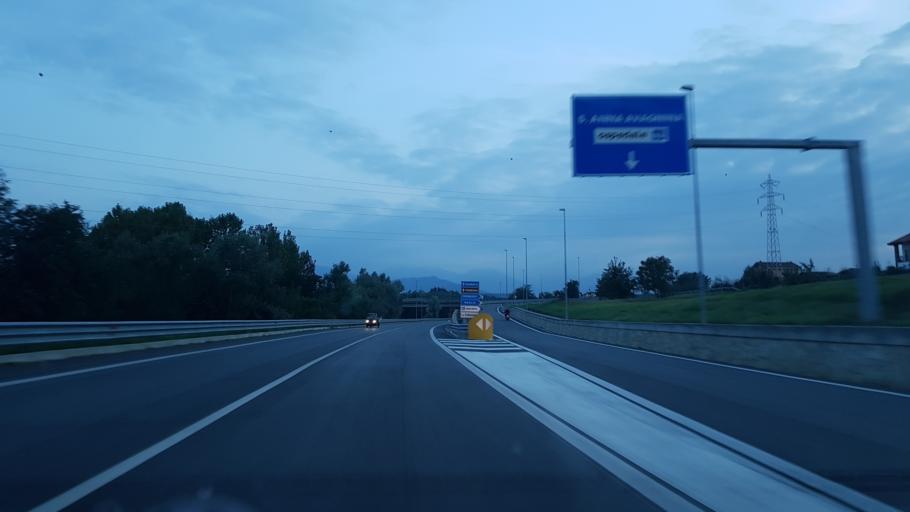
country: IT
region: Piedmont
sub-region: Provincia di Cuneo
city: Mondovi
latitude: 44.3931
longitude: 7.7968
